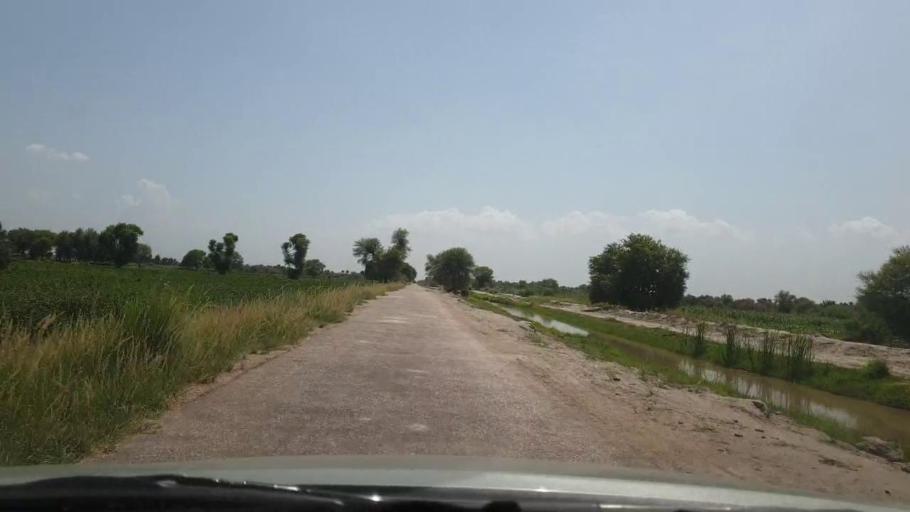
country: PK
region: Sindh
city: Pano Aqil
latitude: 27.7359
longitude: 69.0973
